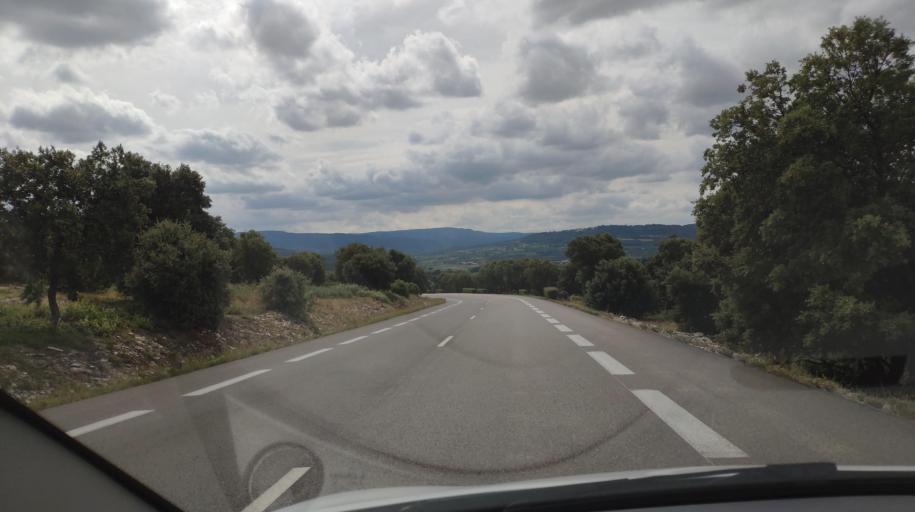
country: FR
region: Provence-Alpes-Cote d'Azur
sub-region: Departement du Vaucluse
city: Villes-sur-Auzon
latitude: 44.0634
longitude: 5.2448
